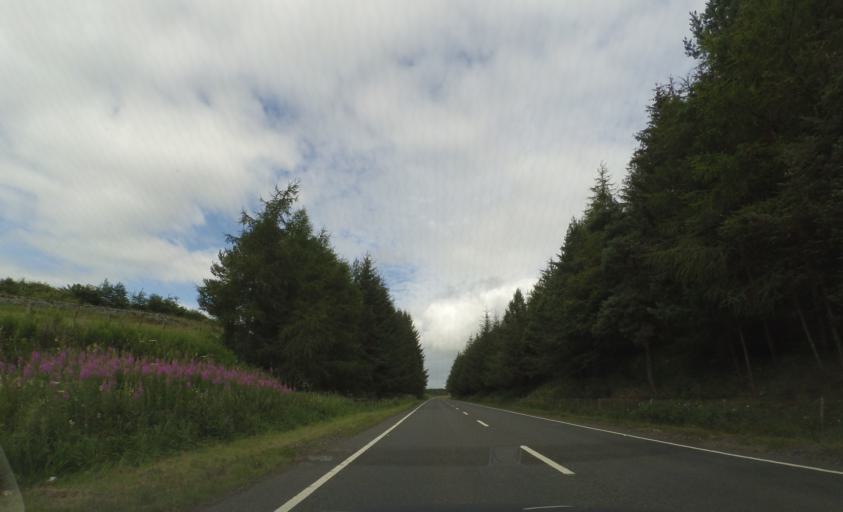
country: GB
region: Scotland
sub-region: The Scottish Borders
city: Selkirk
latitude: 55.5048
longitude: -2.8373
